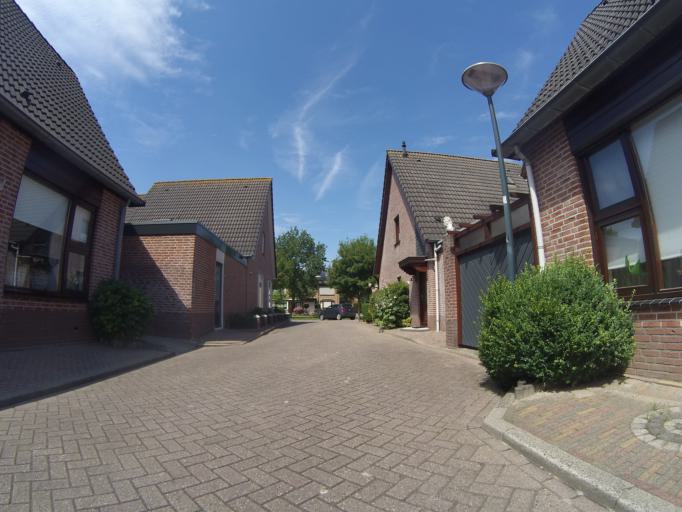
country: NL
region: Utrecht
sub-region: Gemeente Bunschoten
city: Spakenburg
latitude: 52.2547
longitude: 5.3751
